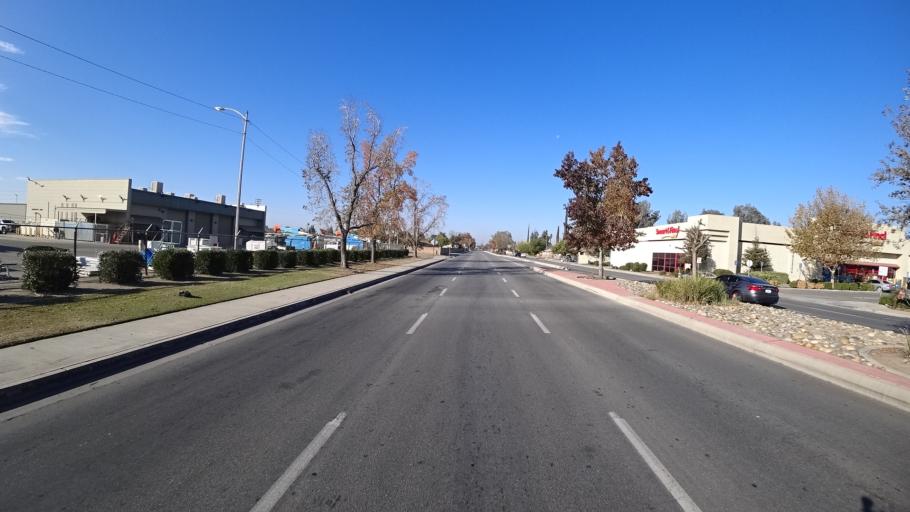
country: US
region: California
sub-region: Kern County
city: Bakersfield
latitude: 35.3176
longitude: -119.0402
